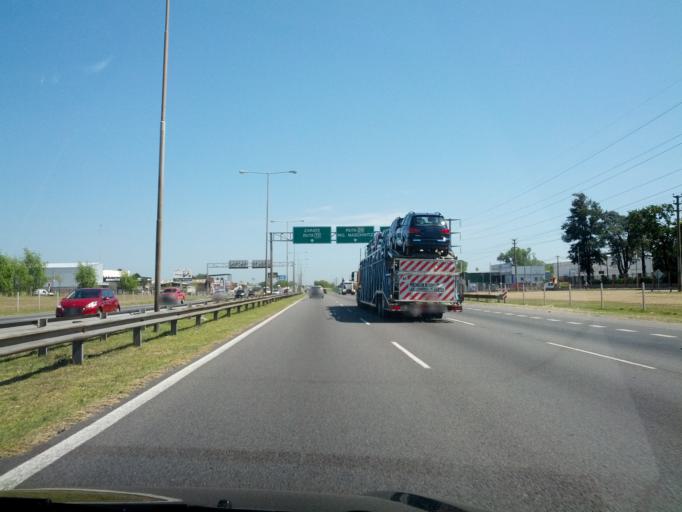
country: AR
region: Buenos Aires
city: Santa Catalina - Dique Lujan
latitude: -34.4144
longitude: -58.7249
